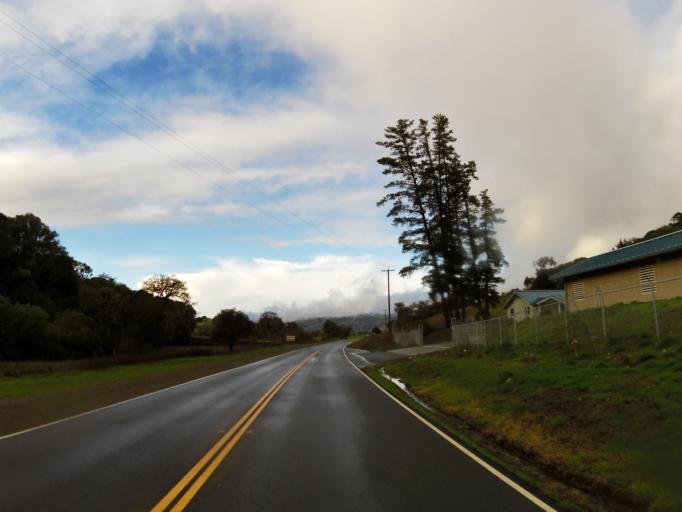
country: US
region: California
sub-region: Mendocino County
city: Boonville
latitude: 38.9863
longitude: -123.3519
